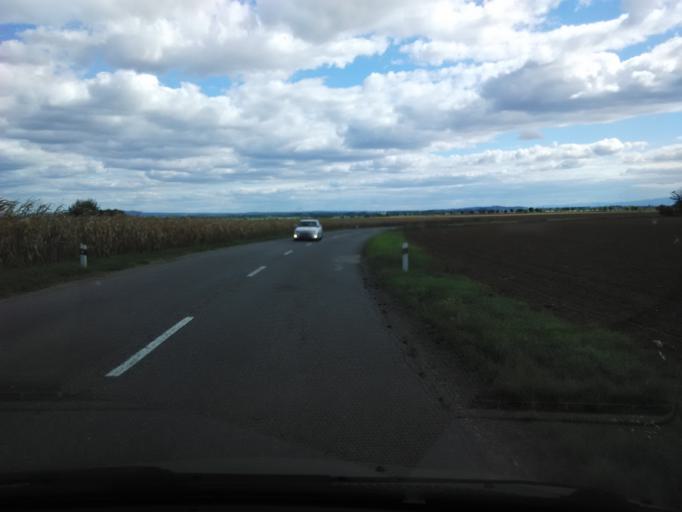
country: SK
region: Nitriansky
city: Tlmace
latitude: 48.2427
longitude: 18.4720
